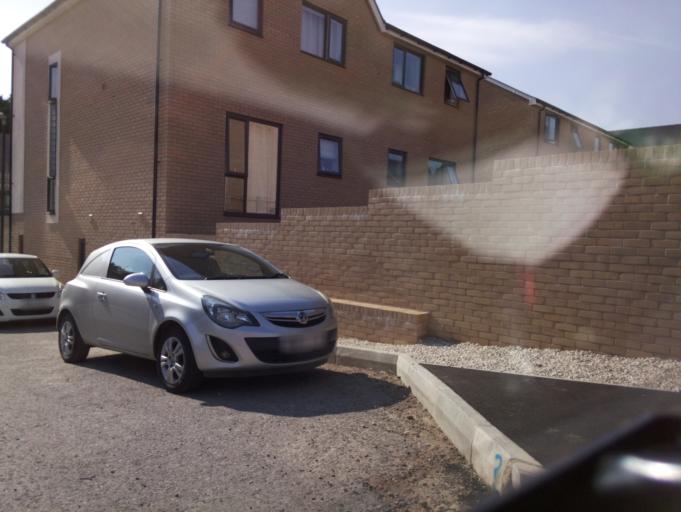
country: GB
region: England
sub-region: Gloucestershire
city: Dursley
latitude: 51.6854
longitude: -2.3512
